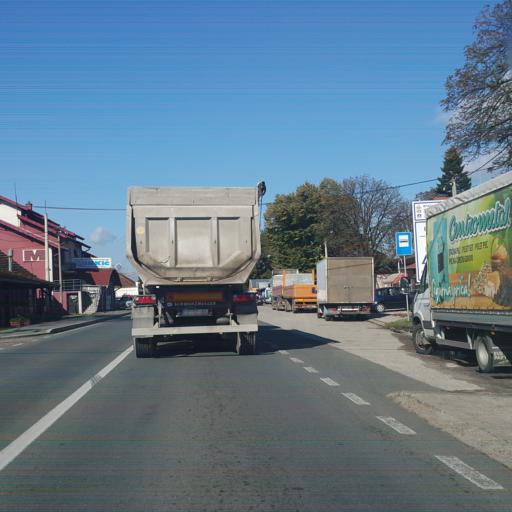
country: RS
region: Central Serbia
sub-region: Raski Okrug
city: Vrnjacka Banja
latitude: 43.6384
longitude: 20.9258
